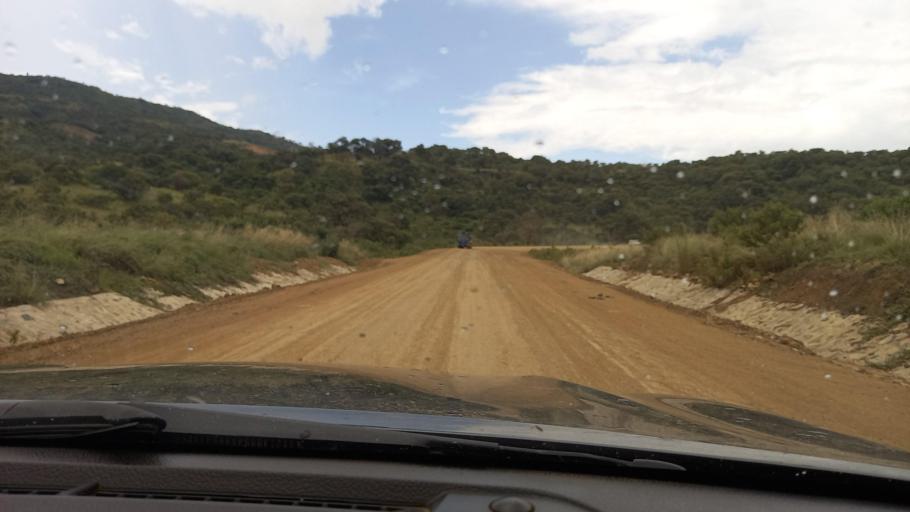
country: ET
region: Southern Nations, Nationalities, and People's Region
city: Mizan Teferi
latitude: 6.1981
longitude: 35.6730
